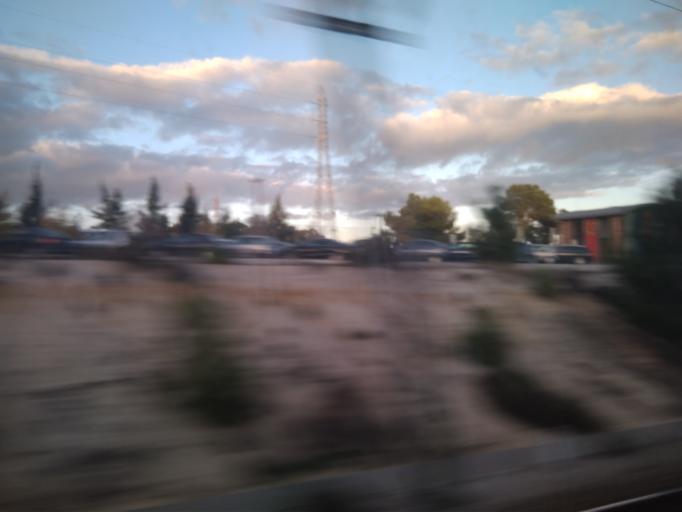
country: PT
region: Setubal
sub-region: Barreiro
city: Santo Antonio da Charneca
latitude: 38.5806
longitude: -9.0432
